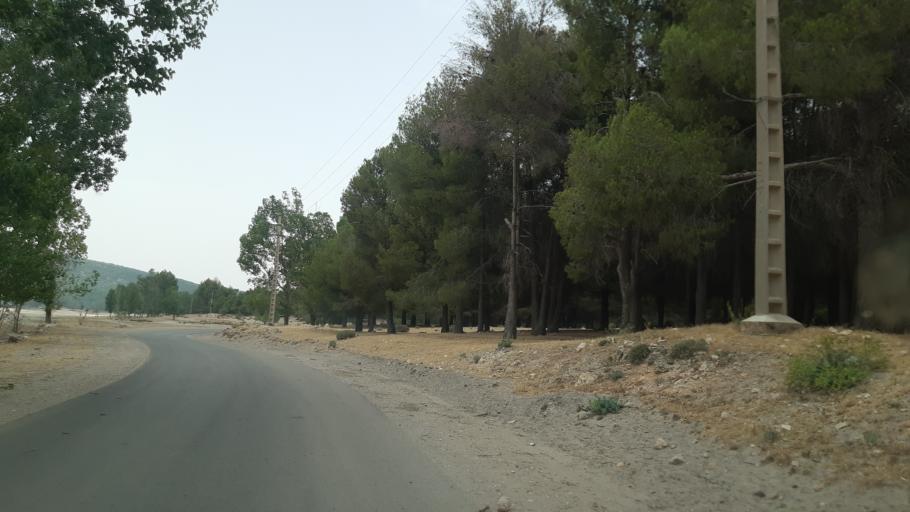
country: MA
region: Meknes-Tafilalet
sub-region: Ifrane
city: Ifrane
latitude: 33.6534
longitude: -5.0280
